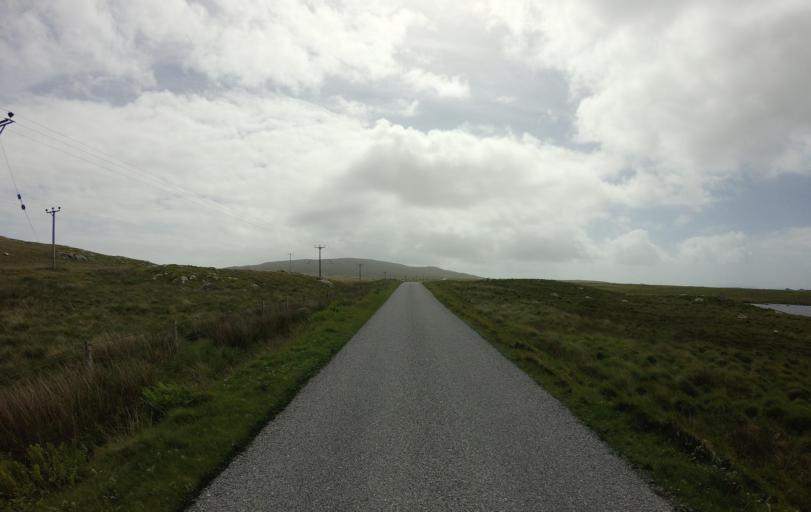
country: GB
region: Scotland
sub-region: Eilean Siar
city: Isle of South Uist
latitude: 57.1422
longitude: -7.3705
